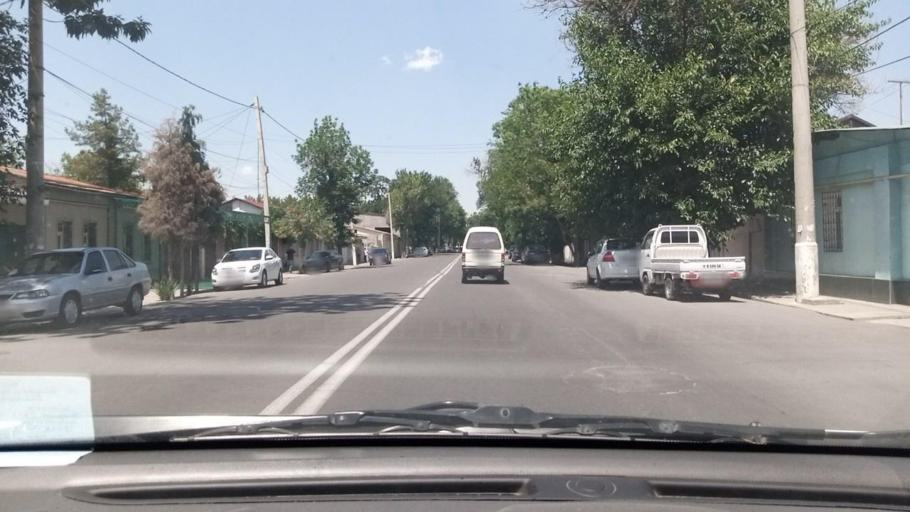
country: UZ
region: Toshkent Shahri
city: Tashkent
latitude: 41.2748
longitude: 69.2763
